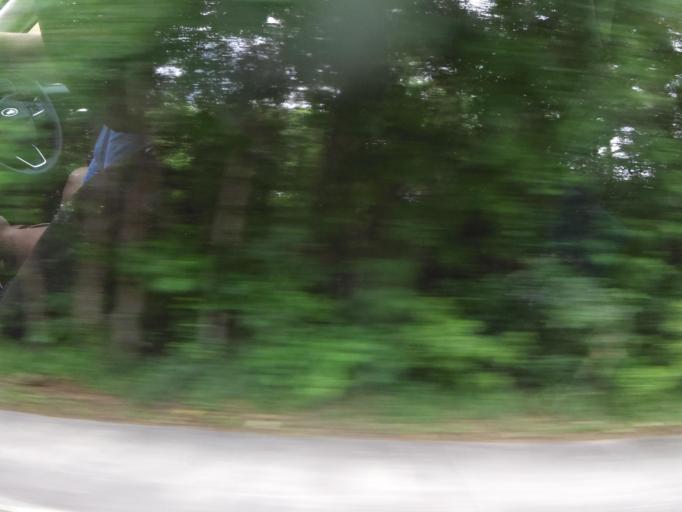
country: US
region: Florida
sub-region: Duval County
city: Jacksonville
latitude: 30.3065
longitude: -81.7422
